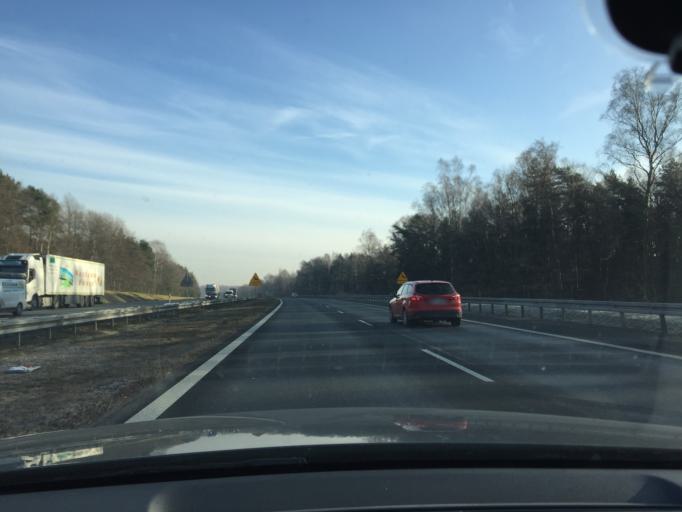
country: PL
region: Silesian Voivodeship
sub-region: Katowice
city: Murcki
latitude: 50.2207
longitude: 19.0995
